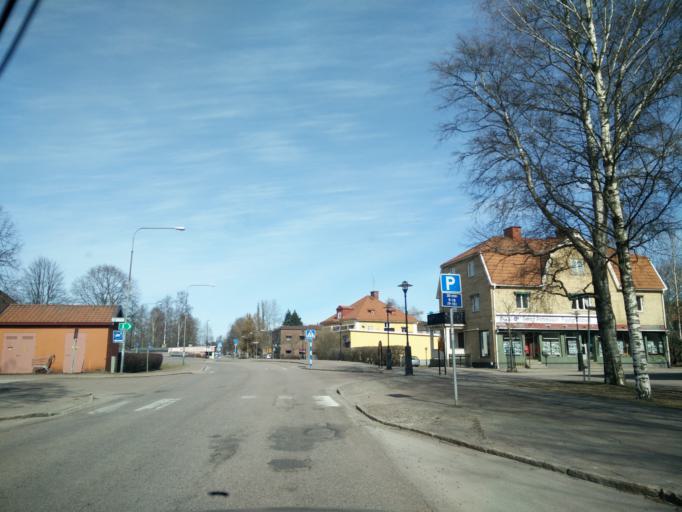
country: SE
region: Vaermland
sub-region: Hagfors Kommun
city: Hagfors
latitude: 60.0316
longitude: 13.6982
